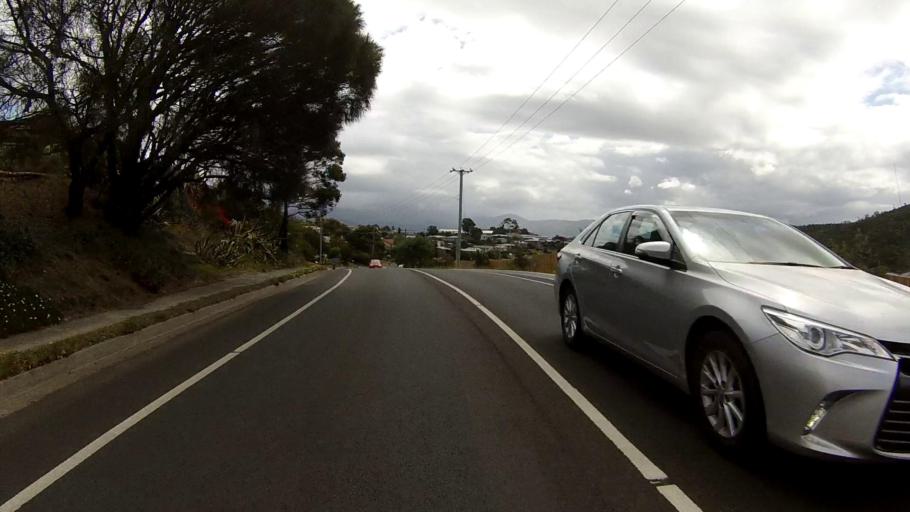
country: AU
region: Tasmania
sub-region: Clarence
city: Warrane
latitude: -42.8574
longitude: 147.4073
